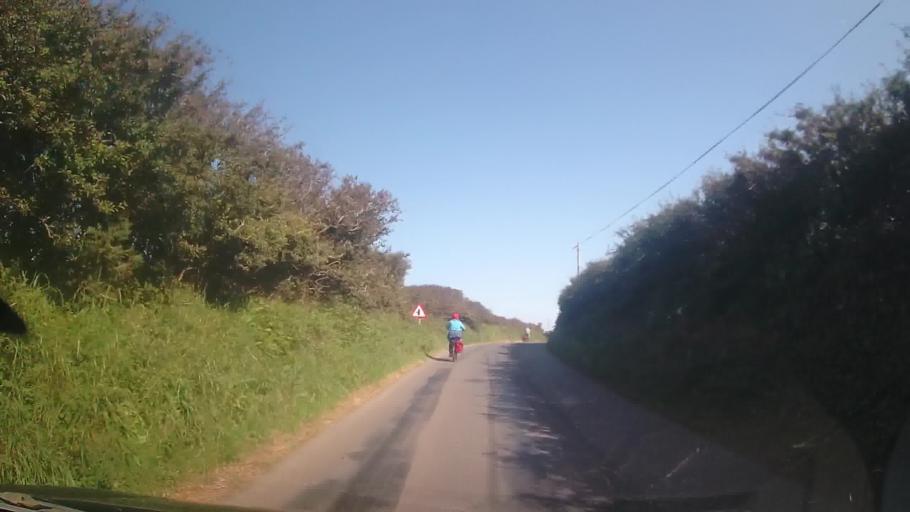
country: GB
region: Wales
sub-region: Pembrokeshire
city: Llanrhian
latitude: 51.9249
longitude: -5.2063
